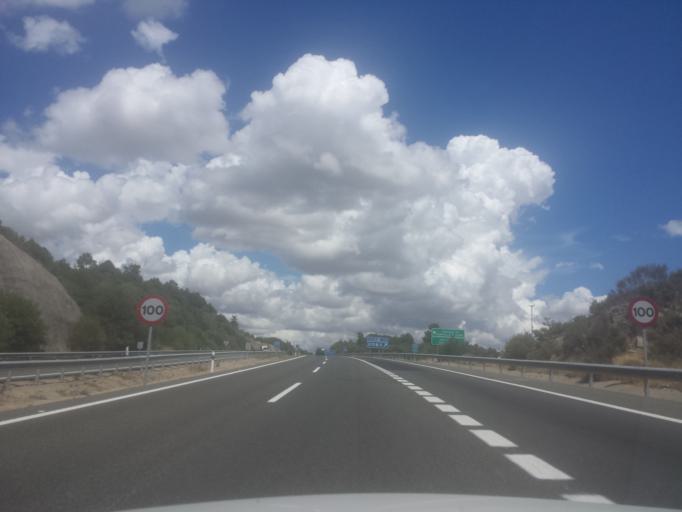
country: ES
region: Castille and Leon
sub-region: Provincia de Salamanca
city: Penacaballera
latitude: 40.3370
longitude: -5.8515
